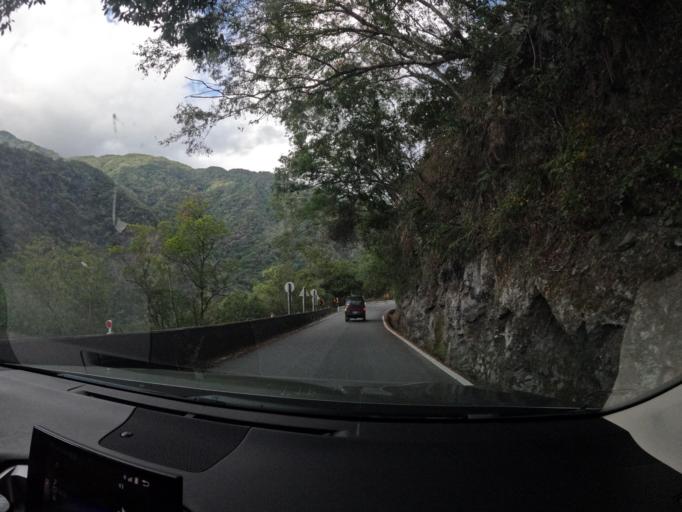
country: TW
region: Taiwan
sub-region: Taitung
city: Taitung
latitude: 23.1398
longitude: 121.0897
